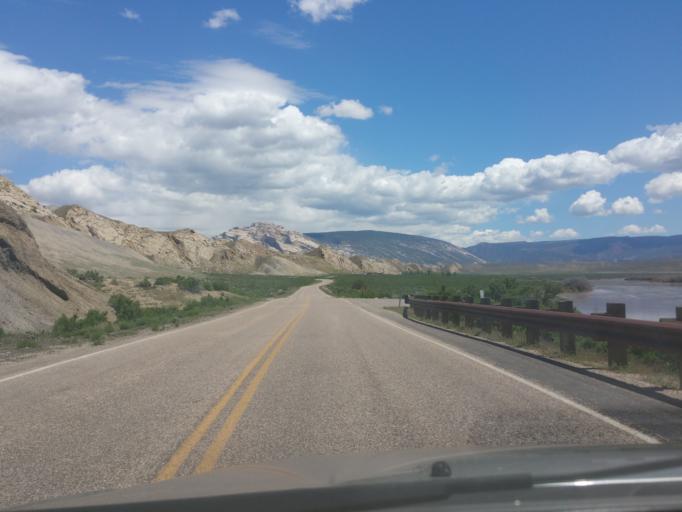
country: US
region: Utah
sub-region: Uintah County
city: Naples
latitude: 40.4373
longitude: -109.3267
